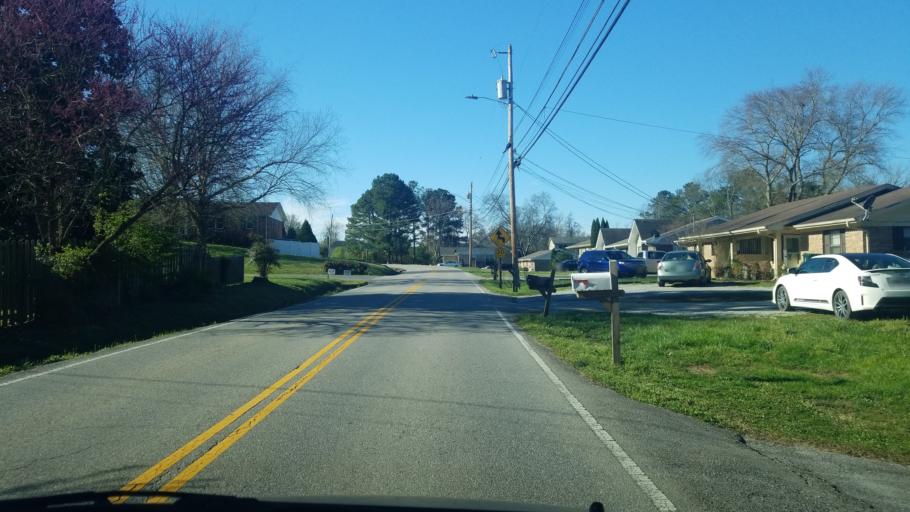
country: US
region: Tennessee
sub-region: Hamilton County
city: East Brainerd
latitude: 35.0225
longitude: -85.1724
